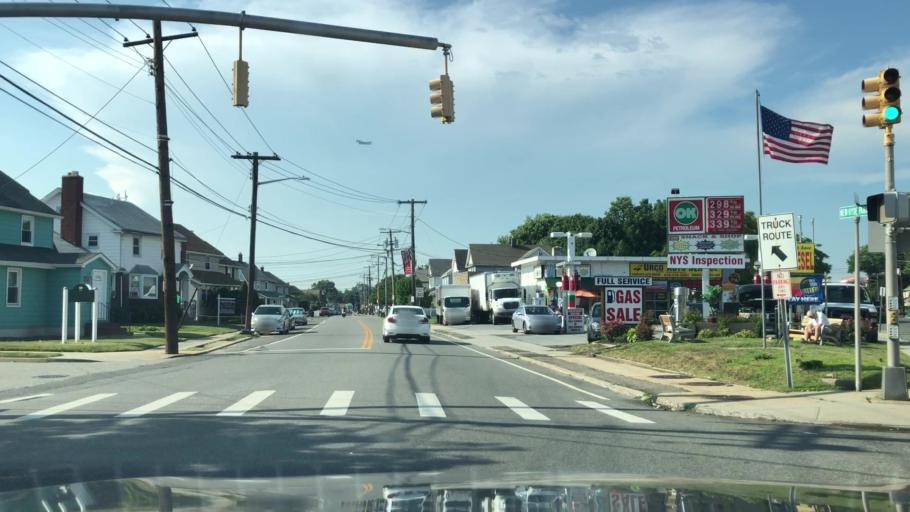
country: US
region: New York
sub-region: Nassau County
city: Franklin Square
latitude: 40.7087
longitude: -73.6755
